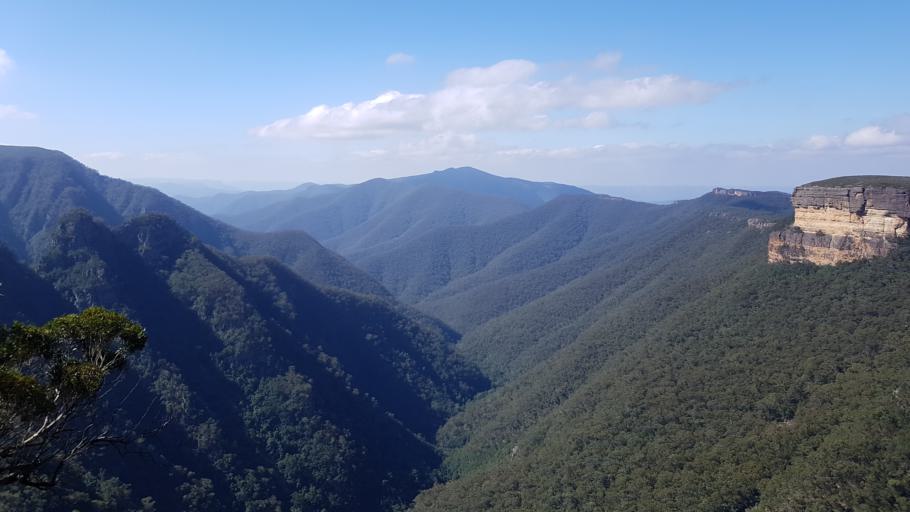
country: AU
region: New South Wales
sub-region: Blue Mountains Municipality
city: Katoomba
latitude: -33.9848
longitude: 150.1116
